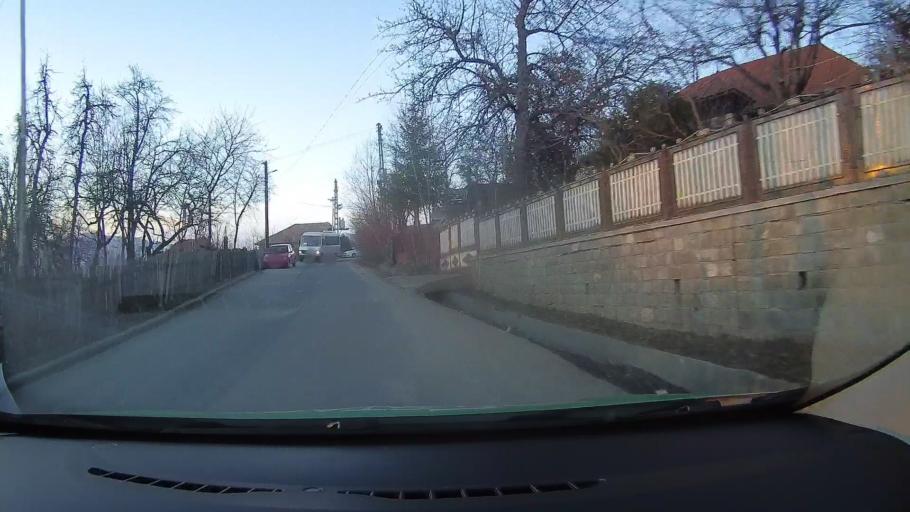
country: RO
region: Prahova
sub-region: Comuna Comarnic
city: Comarnic
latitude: 45.2518
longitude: 25.6432
